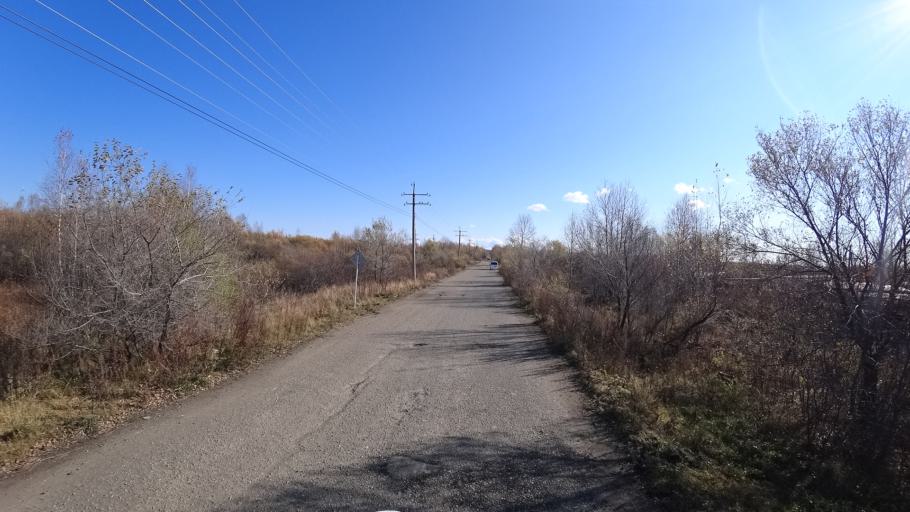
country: RU
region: Khabarovsk Krai
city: Amursk
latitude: 50.1051
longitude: 136.5188
